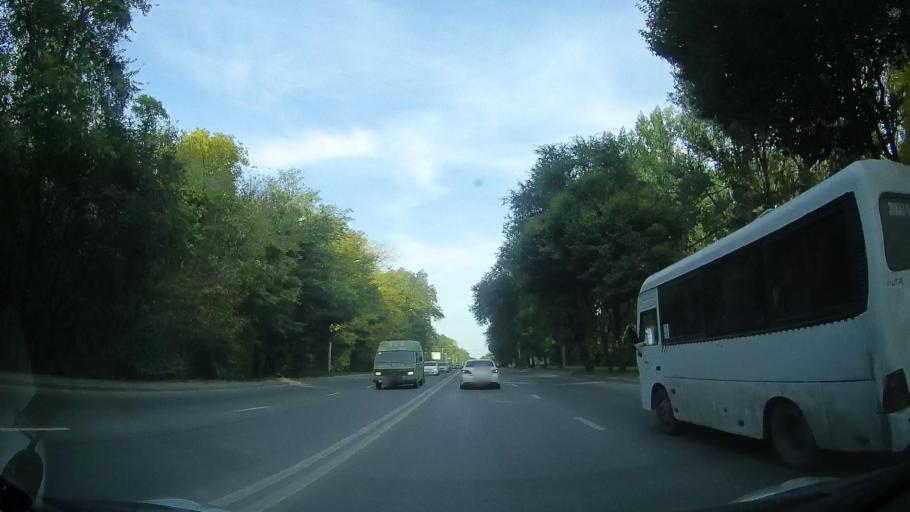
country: RU
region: Rostov
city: Imeni Chkalova
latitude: 47.2777
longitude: 39.7801
